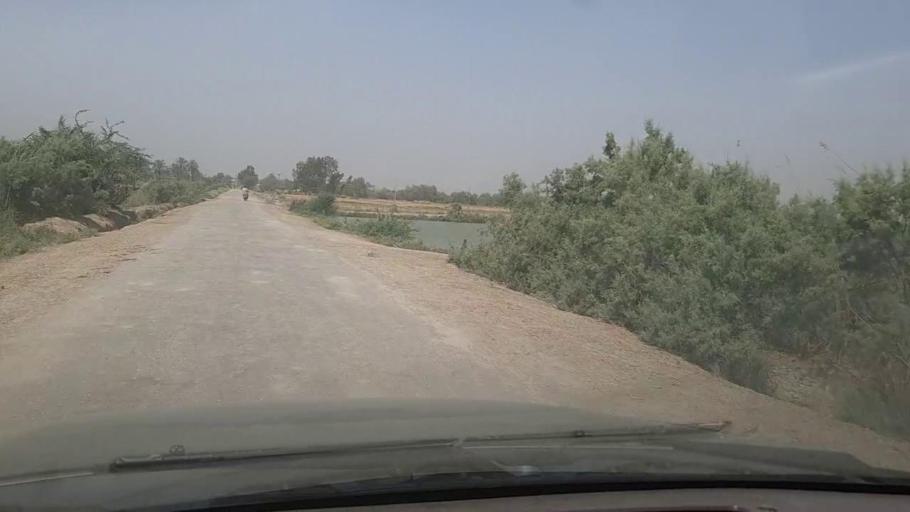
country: PK
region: Sindh
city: Madeji
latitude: 27.7977
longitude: 68.4290
